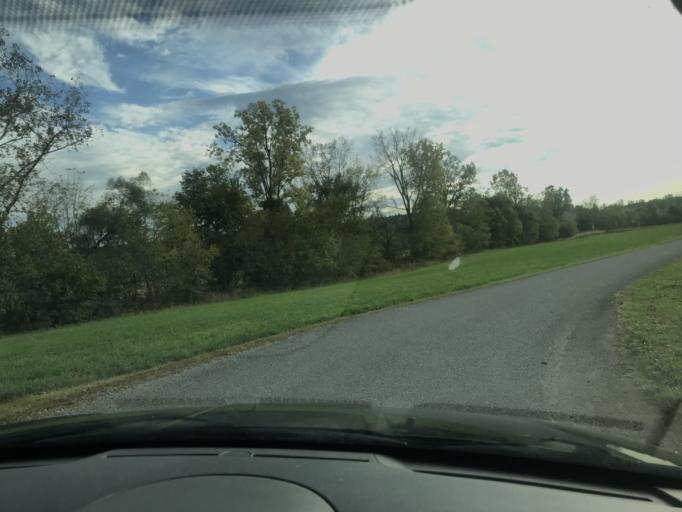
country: US
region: Ohio
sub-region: Logan County
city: West Liberty
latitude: 40.2751
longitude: -83.6784
